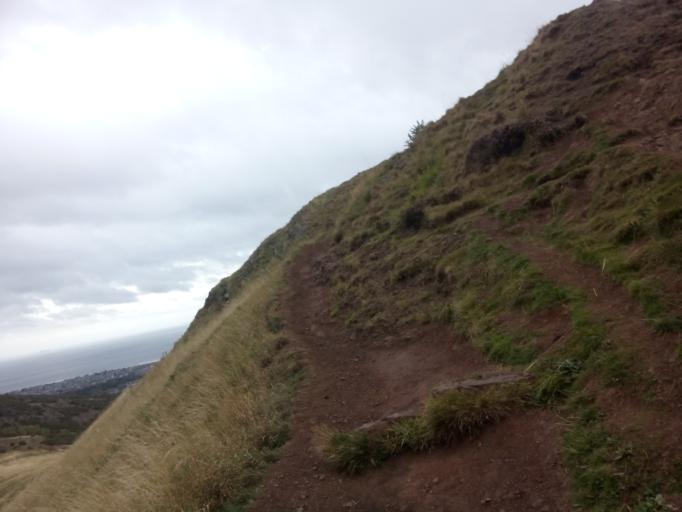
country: GB
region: Scotland
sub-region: West Lothian
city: Seafield
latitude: 55.9449
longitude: -3.1600
